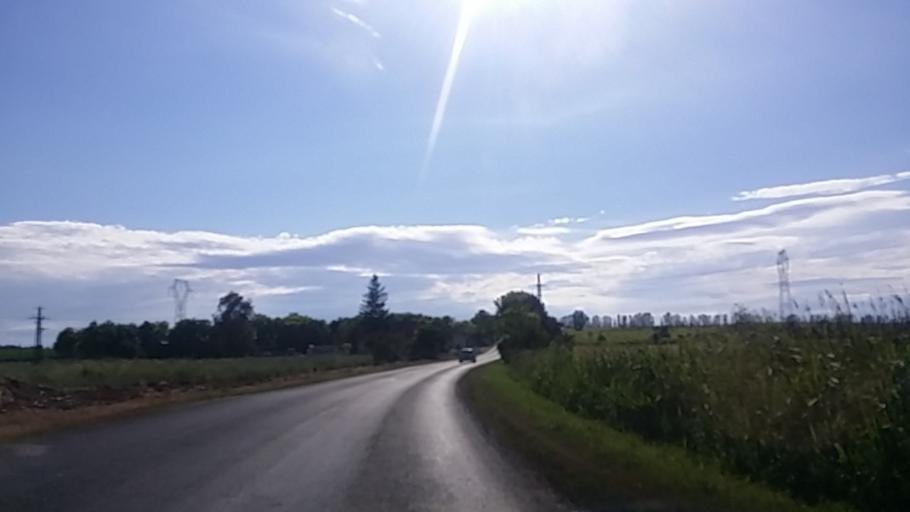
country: HU
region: Pest
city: Kosd
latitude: 47.7684
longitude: 19.2086
